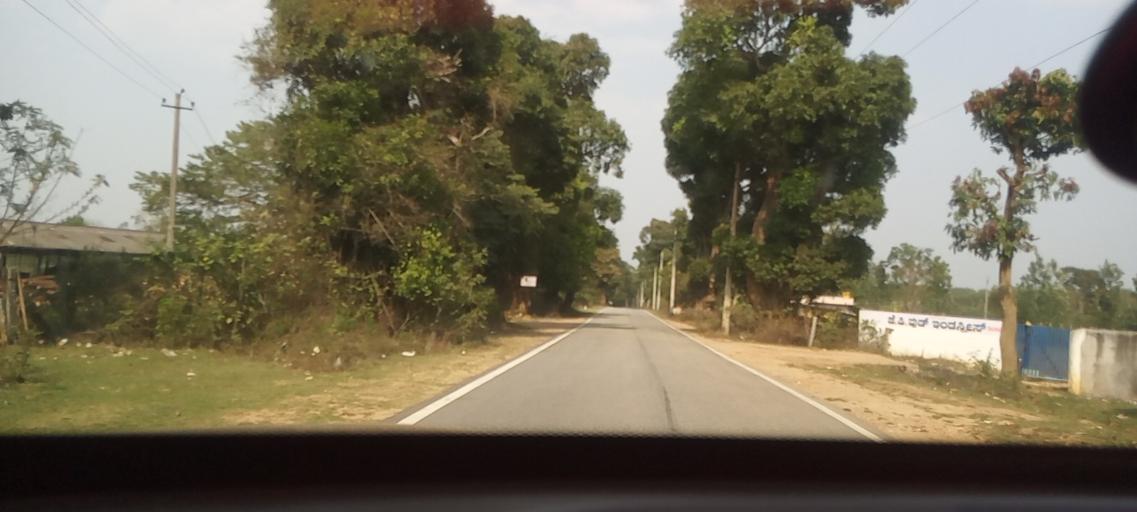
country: IN
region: Karnataka
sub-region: Hassan
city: Belur
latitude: 13.1858
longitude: 75.7843
